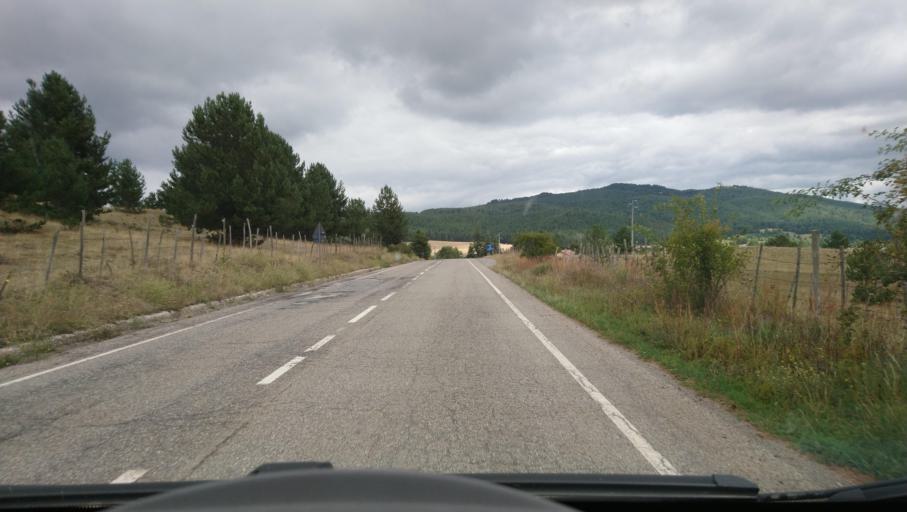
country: IT
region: Calabria
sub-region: Provincia di Cosenza
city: Longobucco
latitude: 39.3123
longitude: 16.5417
